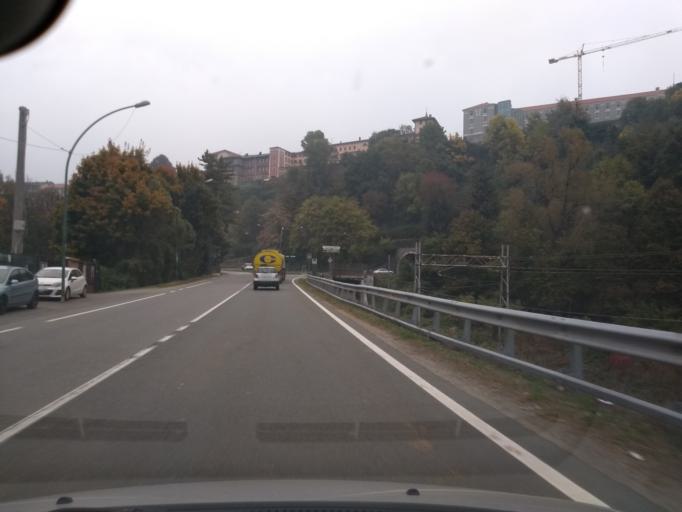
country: IT
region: Piedmont
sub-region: Provincia di Torino
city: Lanzo Torinese
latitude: 45.2691
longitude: 7.4771
